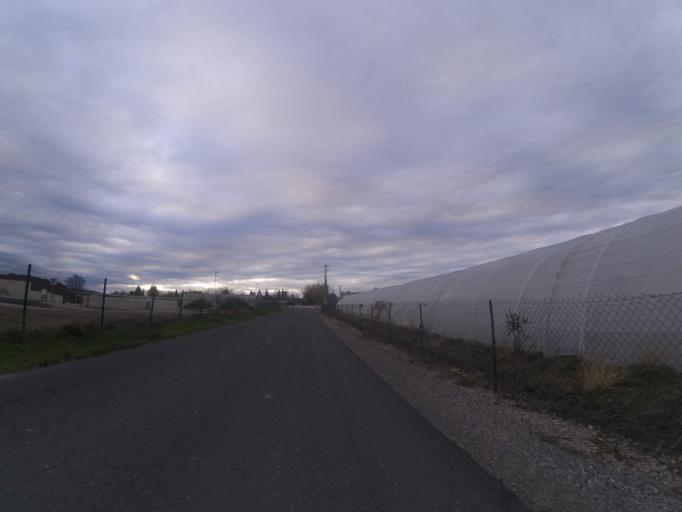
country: FR
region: Languedoc-Roussillon
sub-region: Departement des Pyrenees-Orientales
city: Saint-Esteve
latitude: 42.7025
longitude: 2.8676
